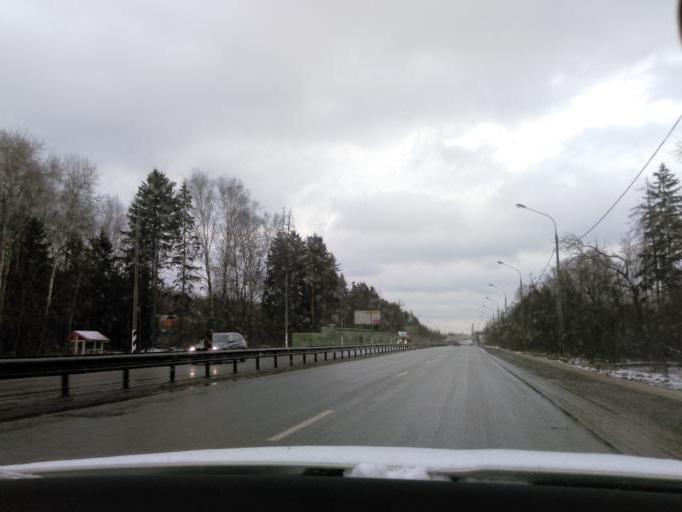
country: RU
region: Moskovskaya
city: Rzhavki
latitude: 56.0067
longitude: 37.2270
